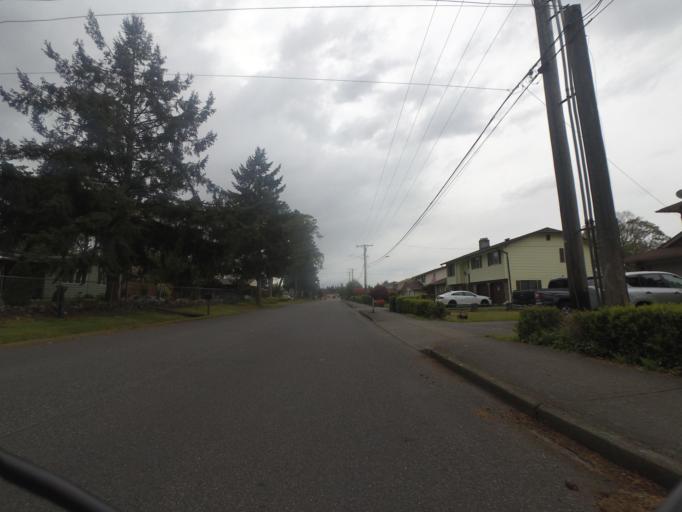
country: US
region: Washington
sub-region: Pierce County
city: Lakewood
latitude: 47.1776
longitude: -122.4790
